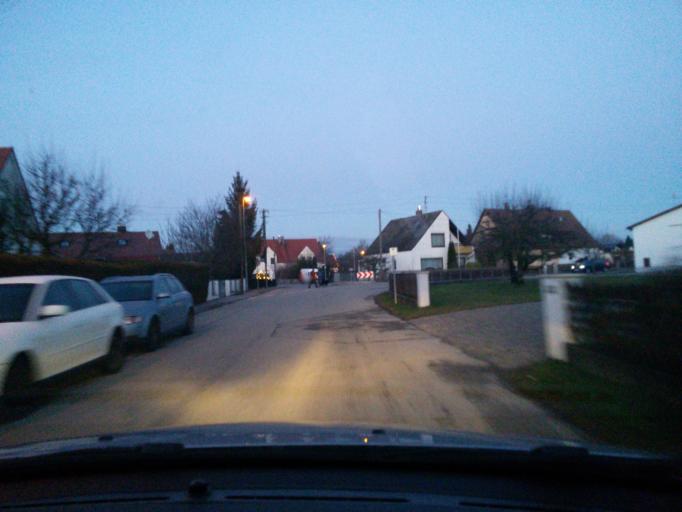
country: DE
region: Bavaria
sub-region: Swabia
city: Grossaitingen
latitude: 48.2080
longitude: 10.7679
